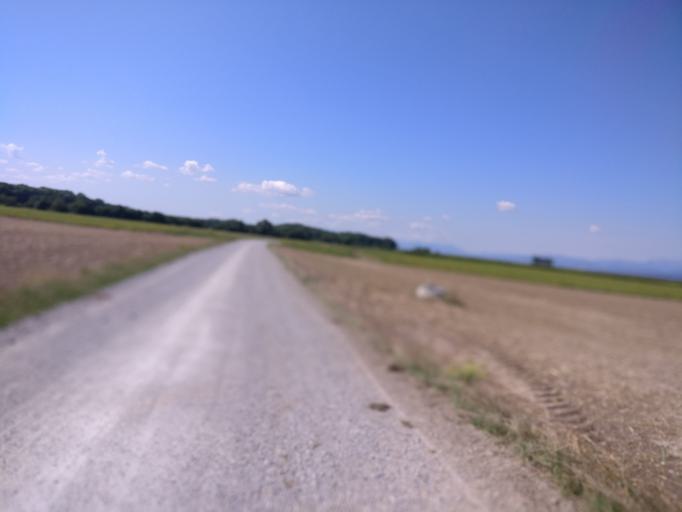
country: AT
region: Lower Austria
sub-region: Politischer Bezirk Wiener Neustadt
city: Ebenfurth
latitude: 47.8773
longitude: 16.3423
